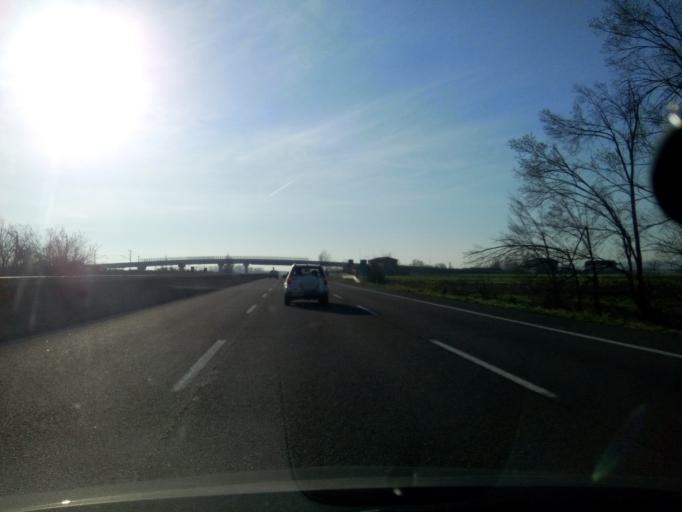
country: IT
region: Emilia-Romagna
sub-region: Provincia di Reggio Emilia
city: Caprara
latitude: 44.7702
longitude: 10.5151
